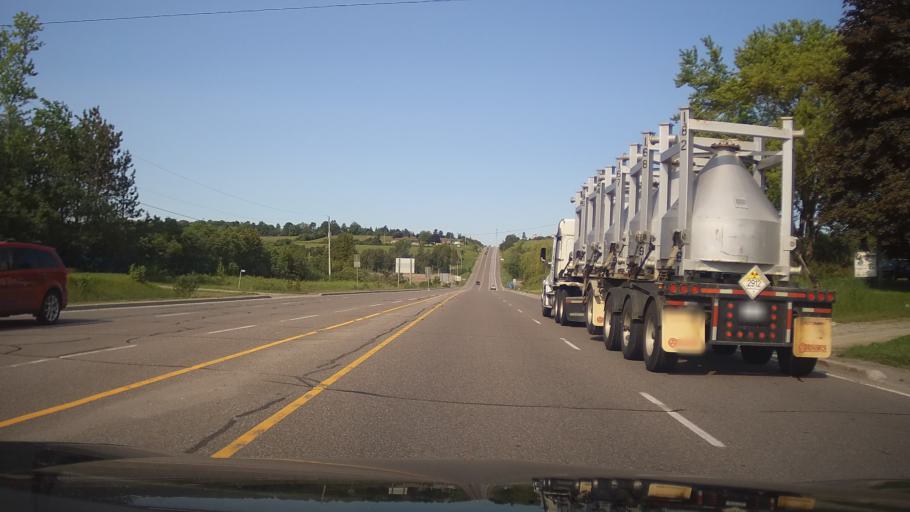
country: CA
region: Ontario
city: Omemee
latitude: 44.3268
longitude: -78.4439
